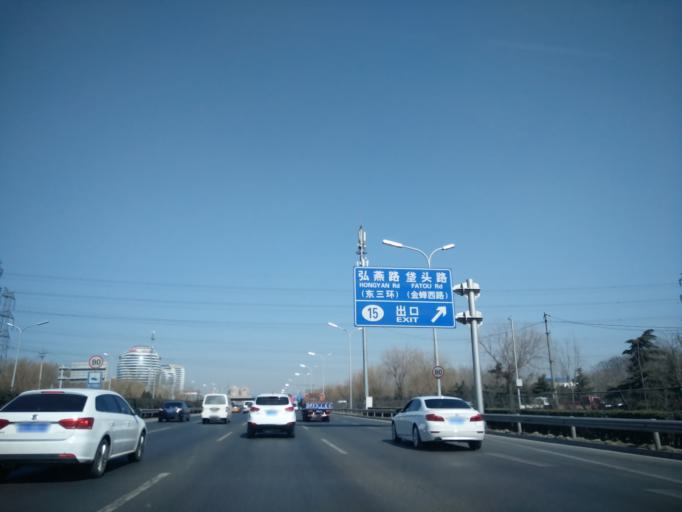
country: CN
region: Beijing
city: Jiugong
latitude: 39.8542
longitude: 116.4803
